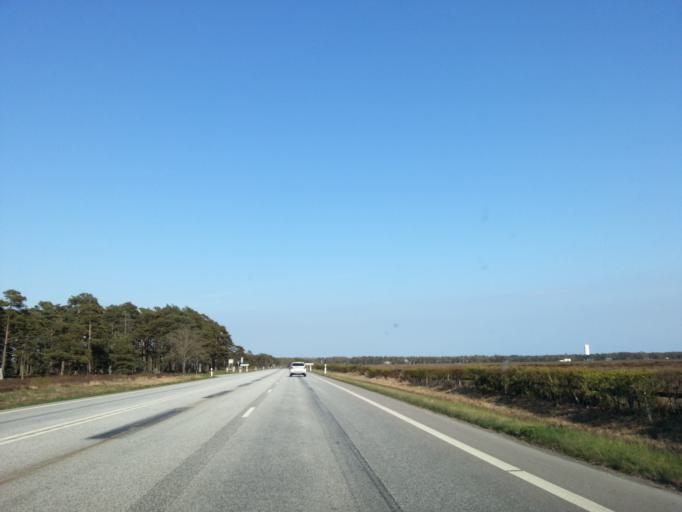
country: SE
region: Skane
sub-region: Vellinge Kommun
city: Ljunghusen
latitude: 55.4050
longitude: 12.8888
